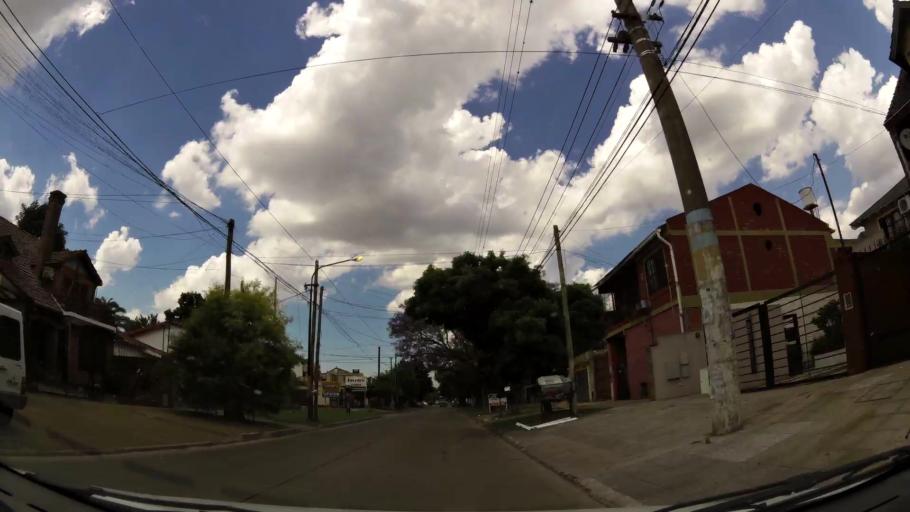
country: AR
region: Buenos Aires
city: Ituzaingo
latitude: -34.6507
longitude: -58.6723
